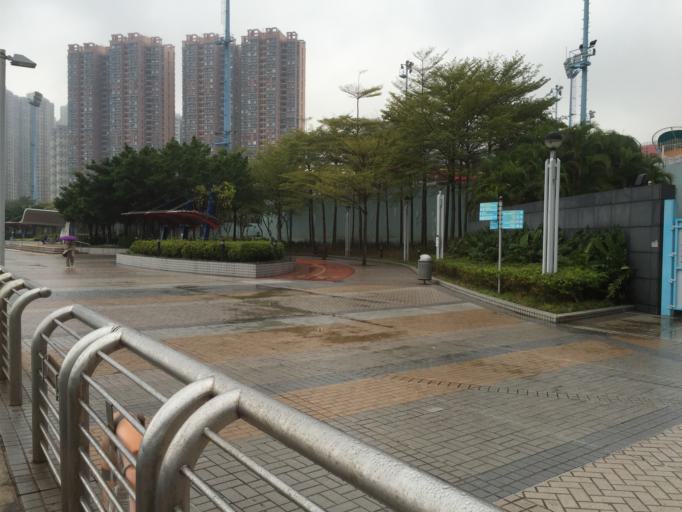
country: HK
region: Tsuen Wan
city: Tsuen Wan
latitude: 22.3577
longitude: 114.1089
